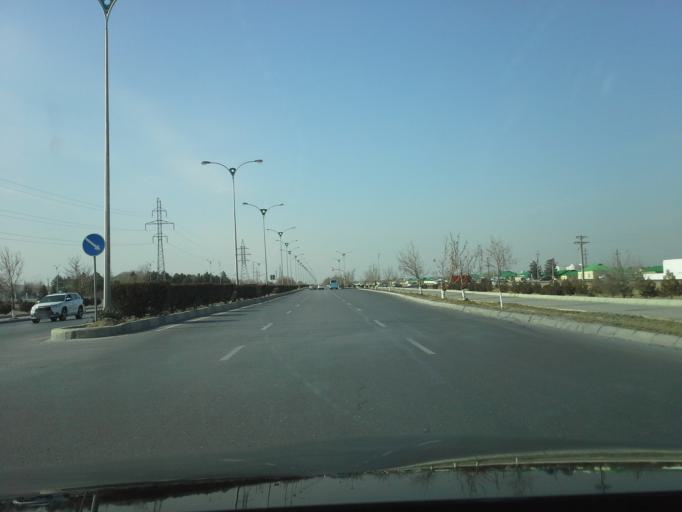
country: TM
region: Ahal
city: Abadan
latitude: 38.0591
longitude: 58.1748
